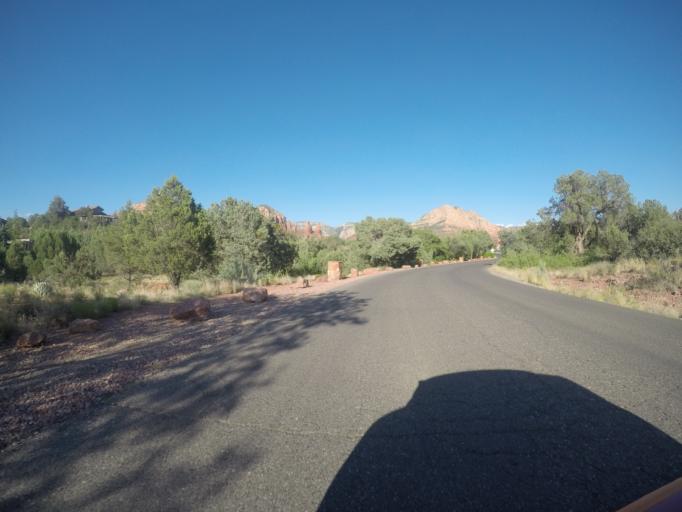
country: US
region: Arizona
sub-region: Coconino County
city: Sedona
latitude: 34.8270
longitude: -111.7803
